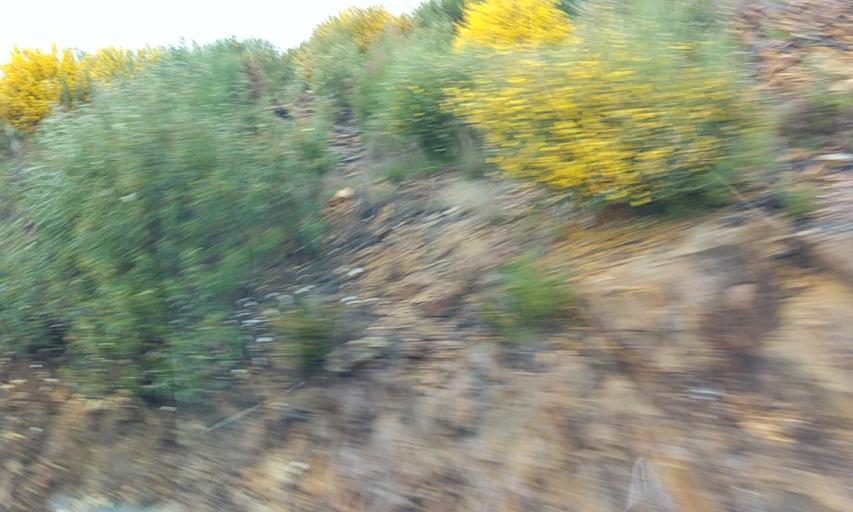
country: ES
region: Extremadura
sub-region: Provincia de Caceres
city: Acebo
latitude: 40.1991
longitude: -6.6762
